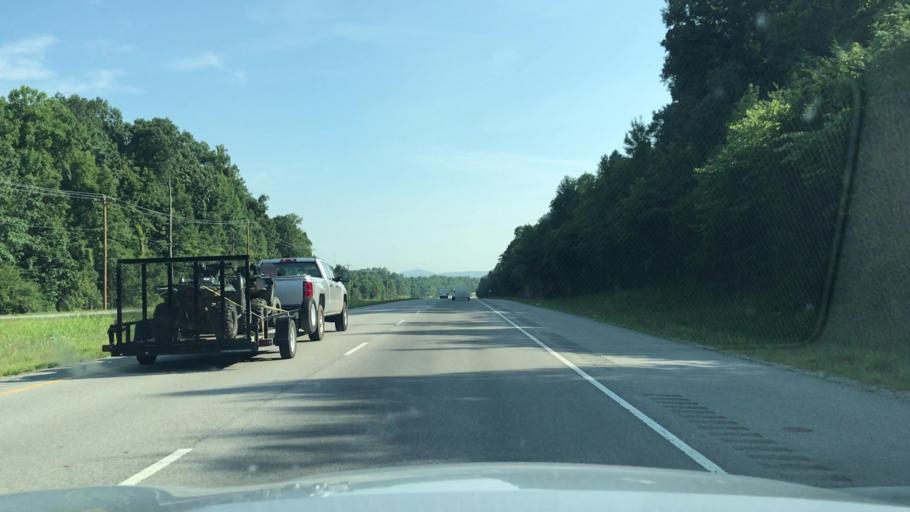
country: US
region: Tennessee
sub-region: Overton County
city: Livingston
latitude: 36.3123
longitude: -85.3646
